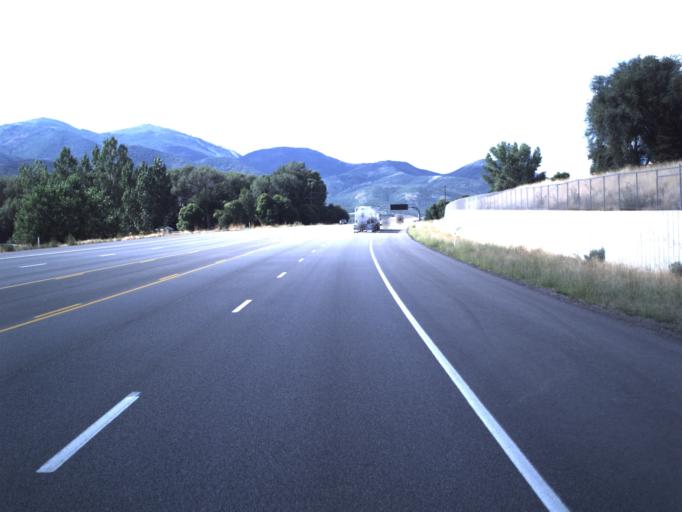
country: US
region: Utah
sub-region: Wasatch County
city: Heber
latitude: 40.5485
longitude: -111.4206
